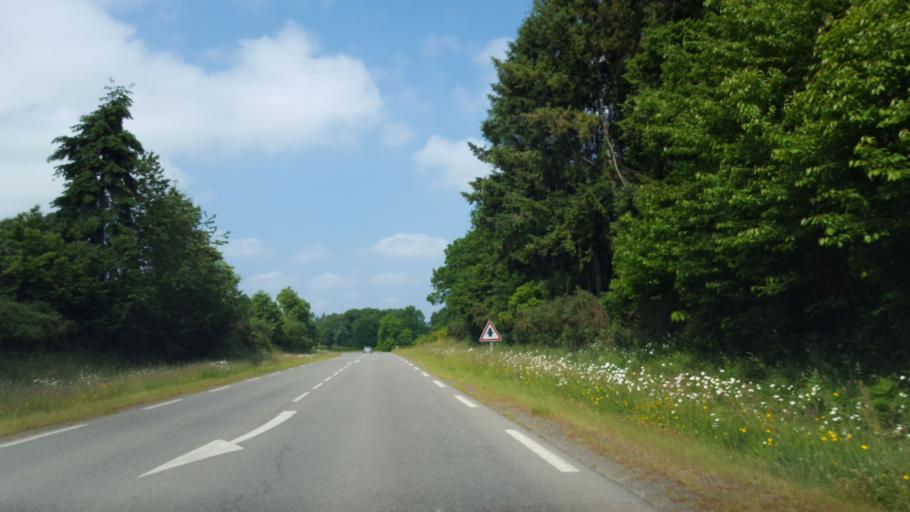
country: FR
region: Brittany
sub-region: Departement d'Ille-et-Vilaine
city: Maure-de-Bretagne
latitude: 47.9236
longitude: -1.9537
